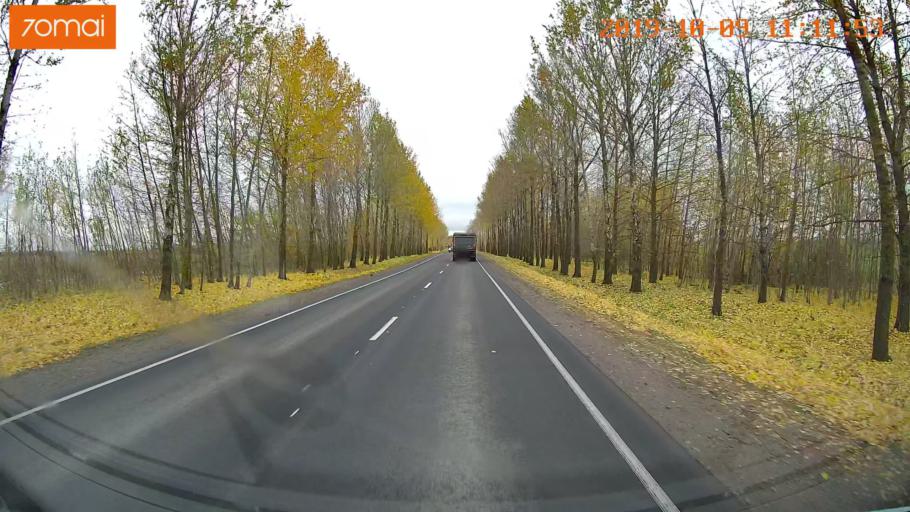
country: RU
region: Vologda
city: Vologda
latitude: 59.1724
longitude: 39.8246
